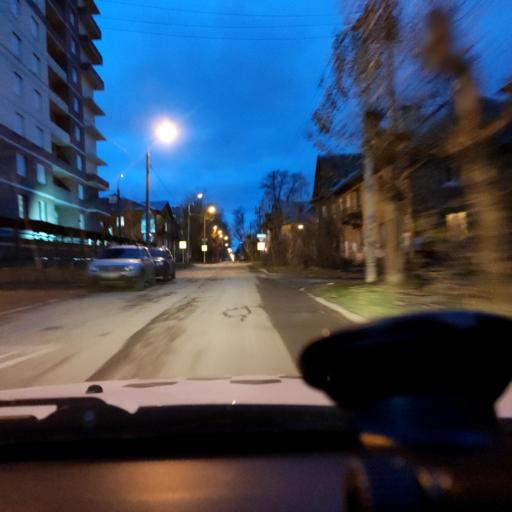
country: RU
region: Perm
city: Kondratovo
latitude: 57.9745
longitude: 56.1807
